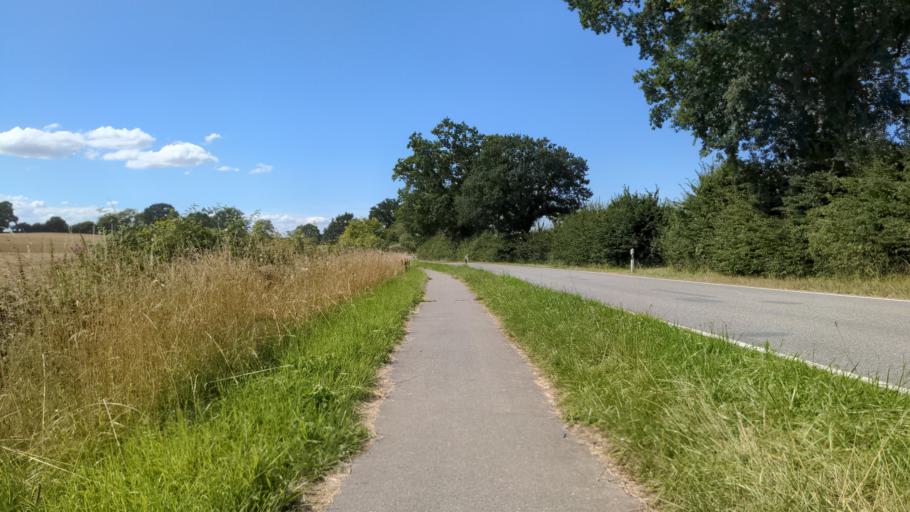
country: DE
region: Schleswig-Holstein
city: Grebin
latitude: 54.1934
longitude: 10.5171
